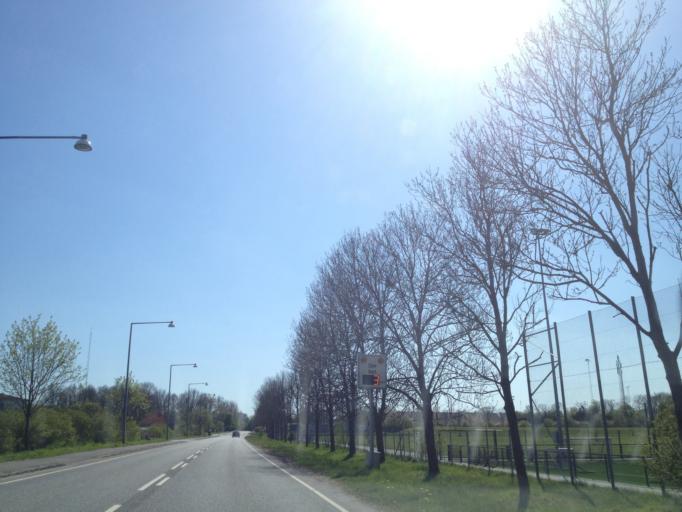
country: DK
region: Zealand
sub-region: Koge Kommune
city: Borup
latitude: 55.5061
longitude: 11.9790
